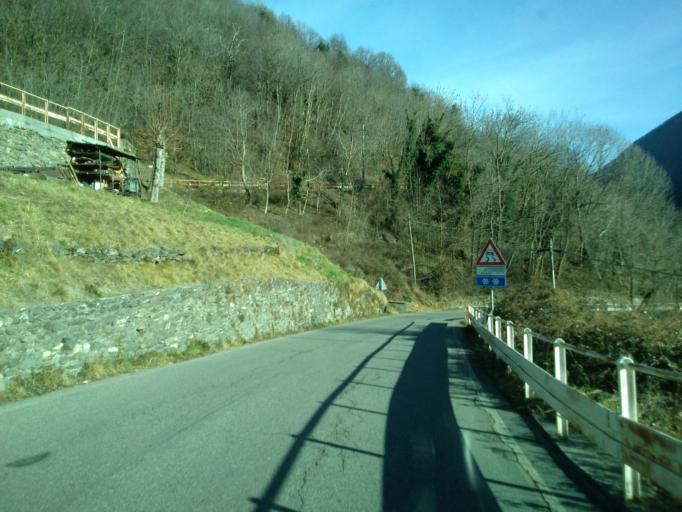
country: IT
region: Lombardy
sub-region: Provincia di Lecco
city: Vestreno
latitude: 46.0835
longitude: 9.3278
